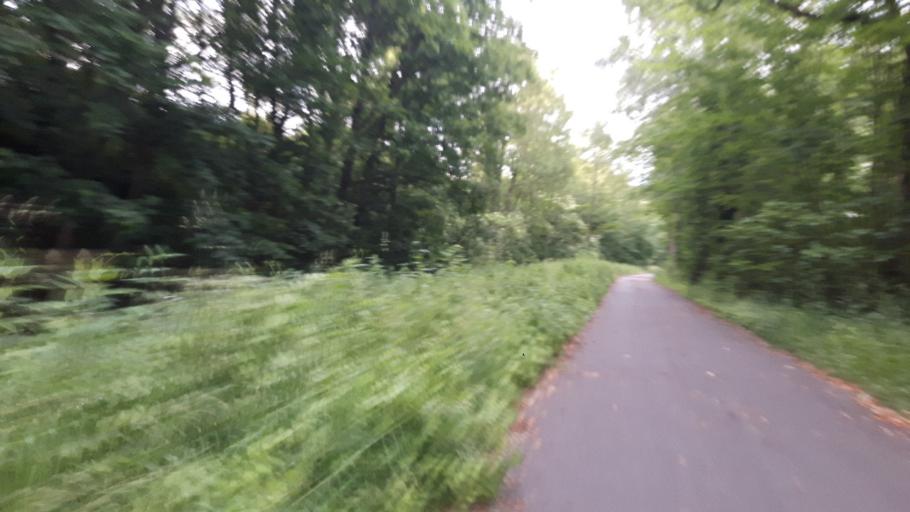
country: DE
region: Brandenburg
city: Gartz
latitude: 53.2146
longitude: 14.4037
